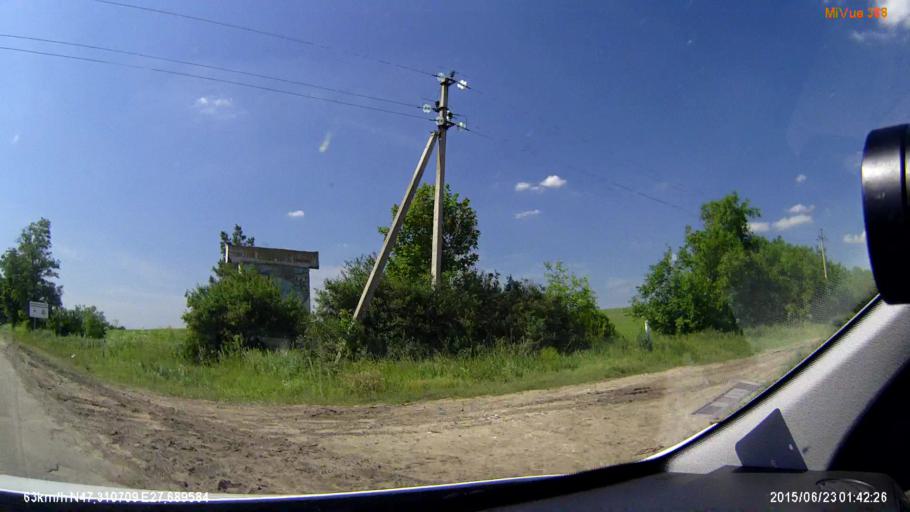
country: RO
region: Iasi
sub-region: Comuna Golaesti
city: Golaesti
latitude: 47.3107
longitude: 27.6898
